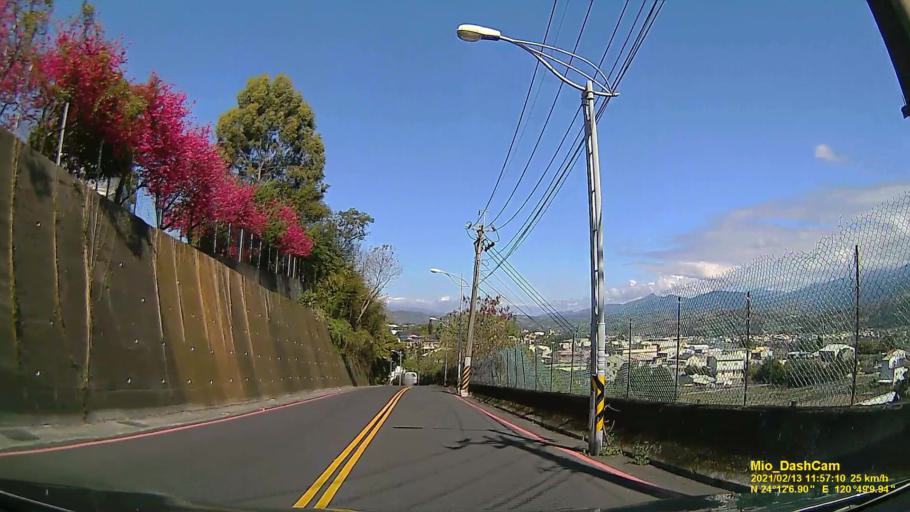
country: TW
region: Taiwan
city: Fengyuan
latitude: 24.2019
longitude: 120.8194
